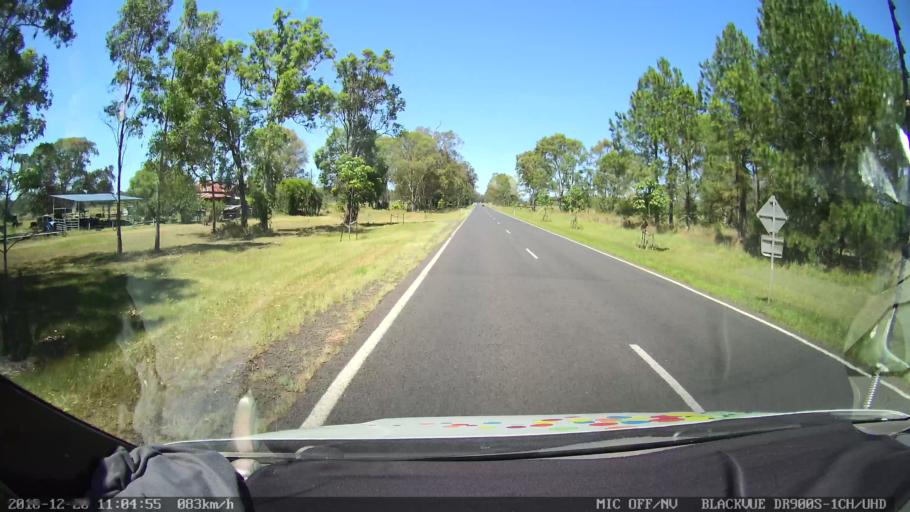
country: AU
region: New South Wales
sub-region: Richmond Valley
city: Casino
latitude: -28.8909
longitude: 153.0457
